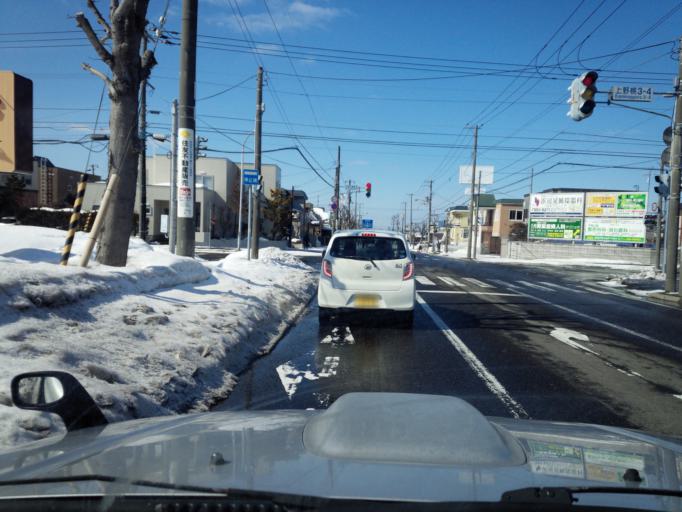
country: JP
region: Hokkaido
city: Kitahiroshima
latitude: 43.0108
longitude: 141.4723
